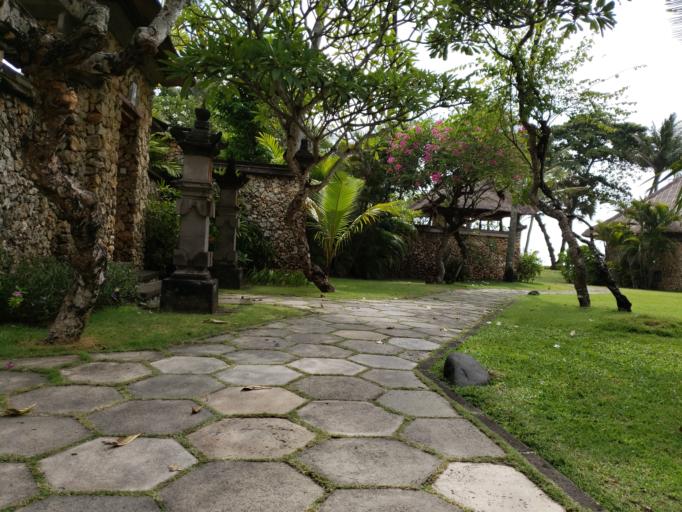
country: ID
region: Bali
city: Kuta
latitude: -8.6896
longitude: 115.1573
